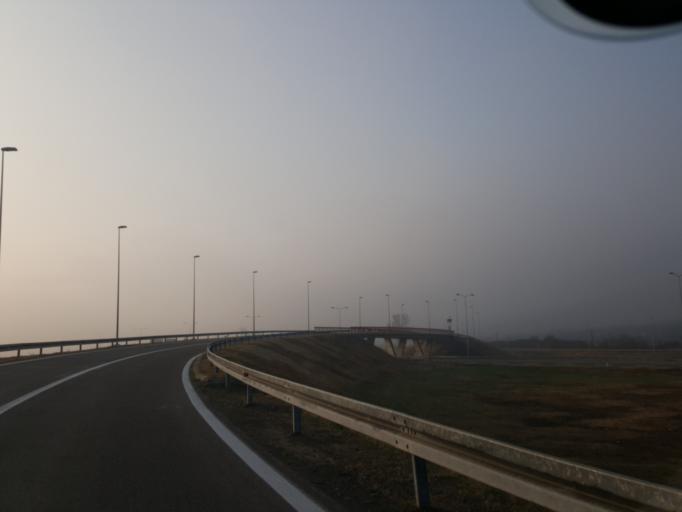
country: RS
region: Central Serbia
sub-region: Jablanicki Okrug
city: Leskovac
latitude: 43.0948
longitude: 21.9386
